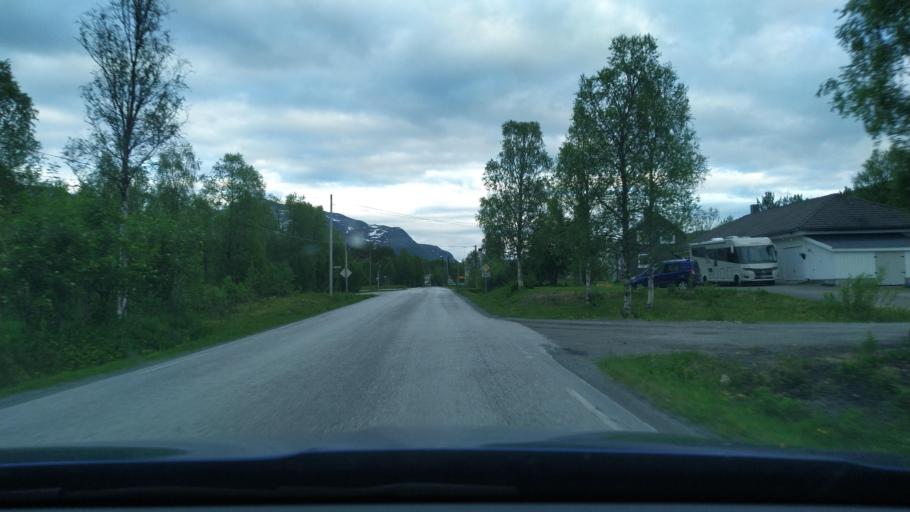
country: NO
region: Troms
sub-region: Dyroy
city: Brostadbotn
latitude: 69.0644
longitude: 17.7355
